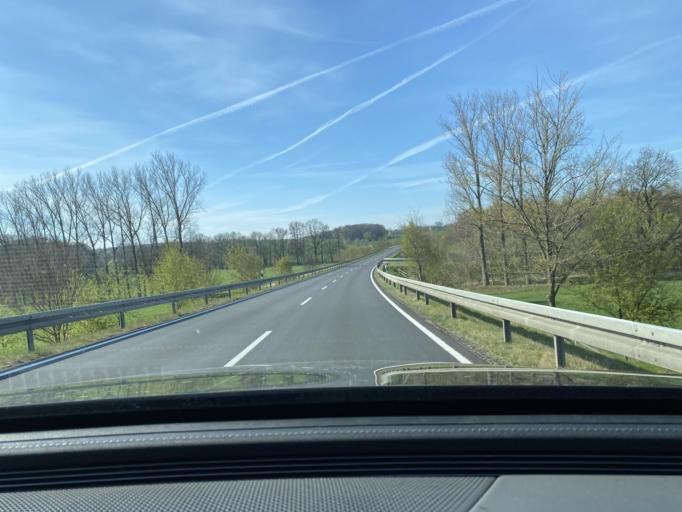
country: DE
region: Saxony
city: Radibor
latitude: 51.2237
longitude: 14.3786
